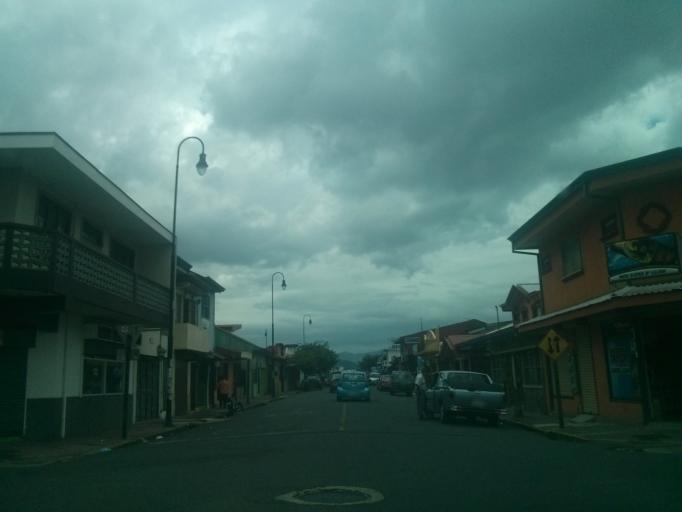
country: CR
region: San Jose
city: San Jose
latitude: 9.9266
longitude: -84.0714
